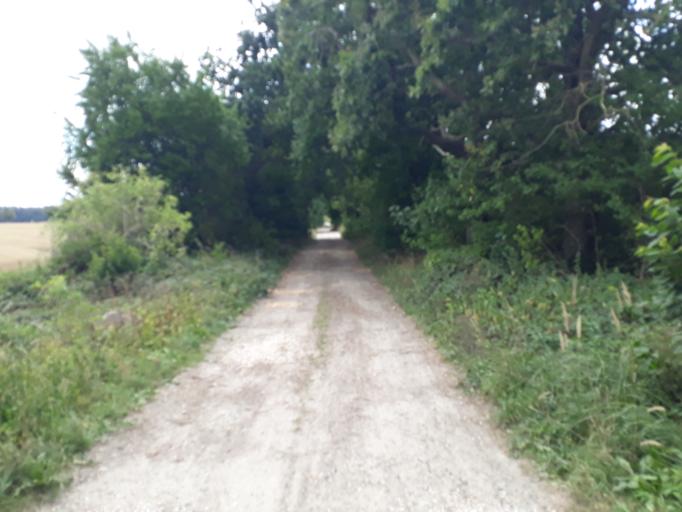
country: DE
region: Mecklenburg-Vorpommern
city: Marlow
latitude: 54.1774
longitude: 12.6052
